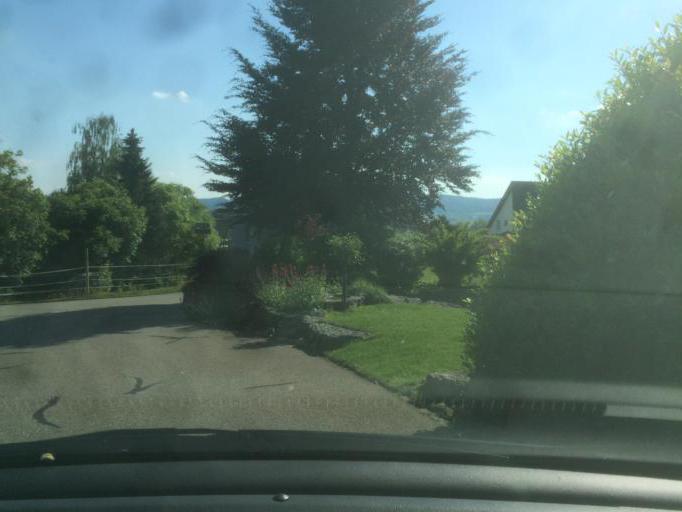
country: CH
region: Zurich
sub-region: Bezirk Uster
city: Uster / Nossikon
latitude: 47.3425
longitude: 8.7274
